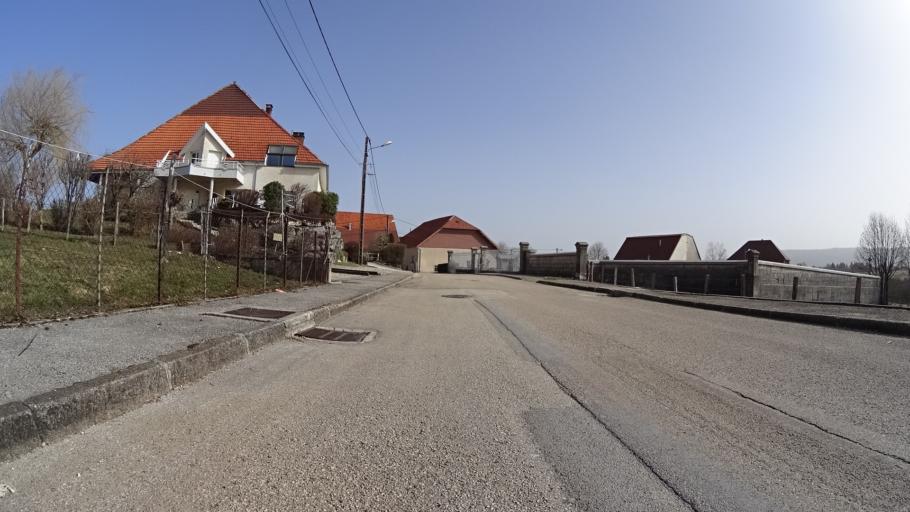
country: FR
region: Franche-Comte
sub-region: Departement du Doubs
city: Frasne
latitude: 46.8578
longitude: 6.1648
